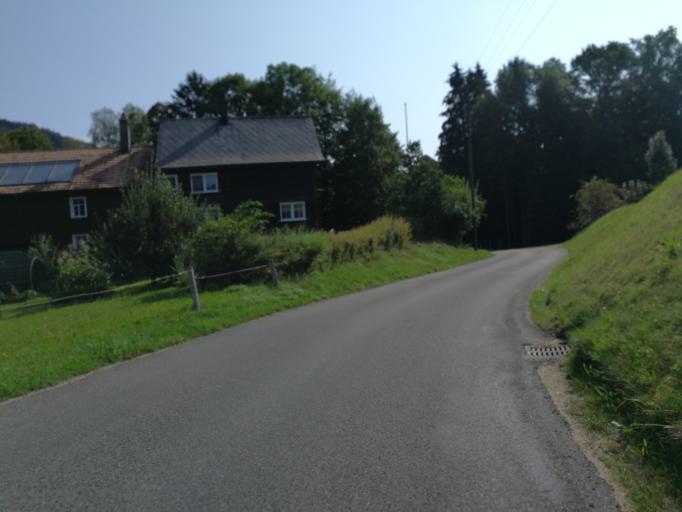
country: CH
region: Saint Gallen
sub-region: Wahlkreis Toggenburg
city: Ebnat-Kappel
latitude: 47.2539
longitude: 9.1398
